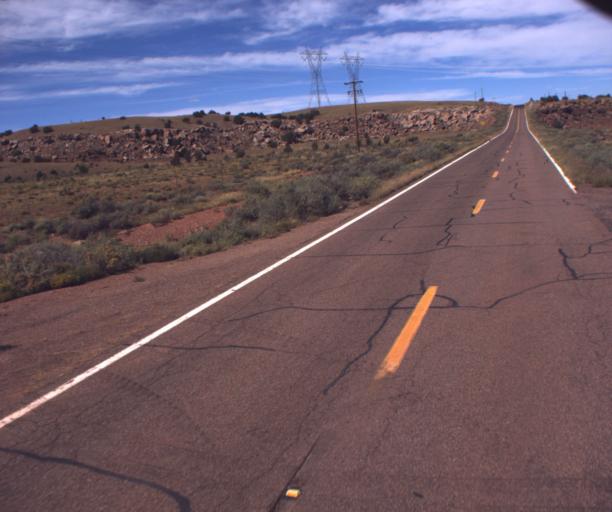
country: US
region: Arizona
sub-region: Apache County
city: Saint Johns
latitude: 34.5491
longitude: -109.6239
